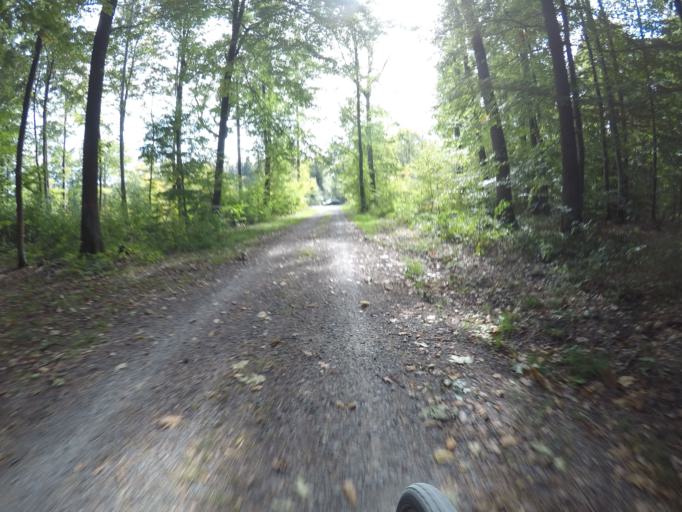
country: DE
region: Baden-Wuerttemberg
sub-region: Regierungsbezirk Stuttgart
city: Hildrizhausen
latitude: 48.6127
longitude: 8.9325
